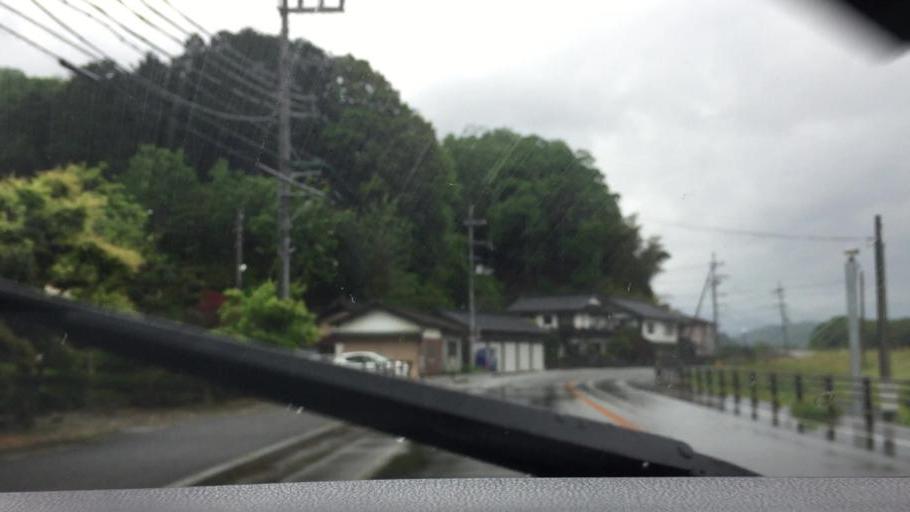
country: JP
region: Hyogo
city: Toyooka
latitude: 35.4828
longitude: 134.8137
